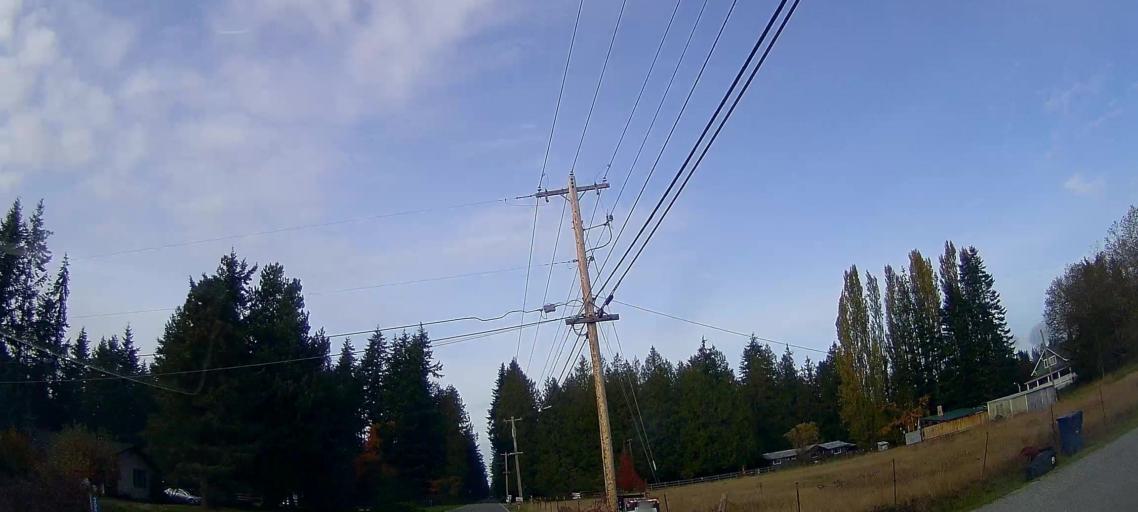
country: US
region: Washington
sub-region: Snohomish County
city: Stanwood
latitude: 48.2758
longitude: -122.3364
